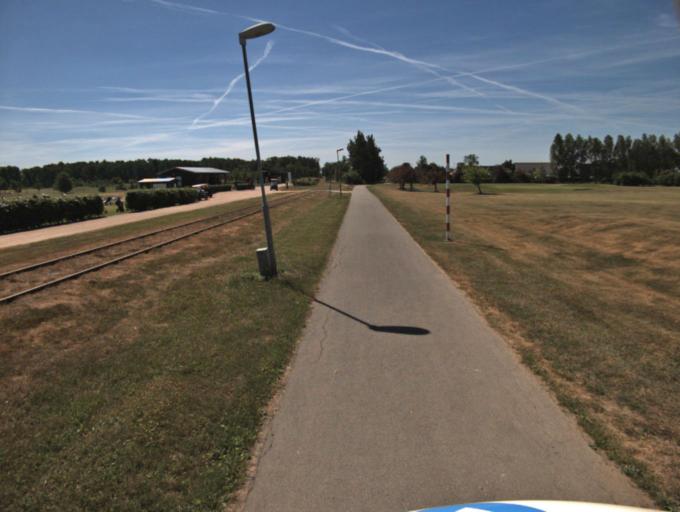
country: SE
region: Skane
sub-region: Kristianstads Kommun
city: Kristianstad
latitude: 56.0638
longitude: 14.0885
